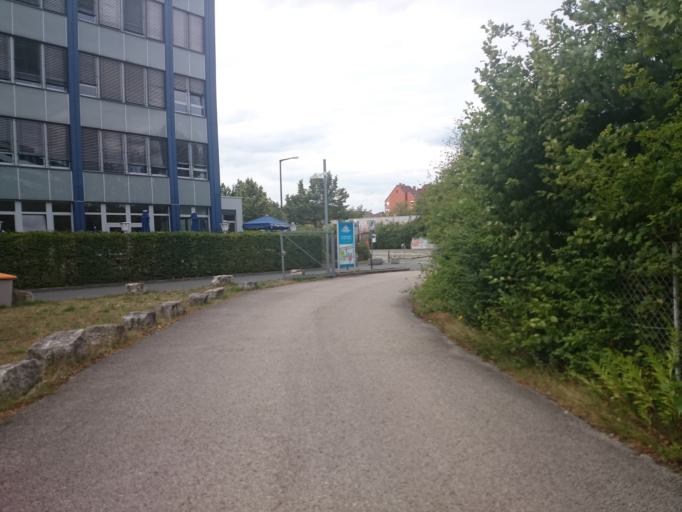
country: DE
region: Bavaria
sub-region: Regierungsbezirk Mittelfranken
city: Wendelstein
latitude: 49.4100
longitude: 11.1294
